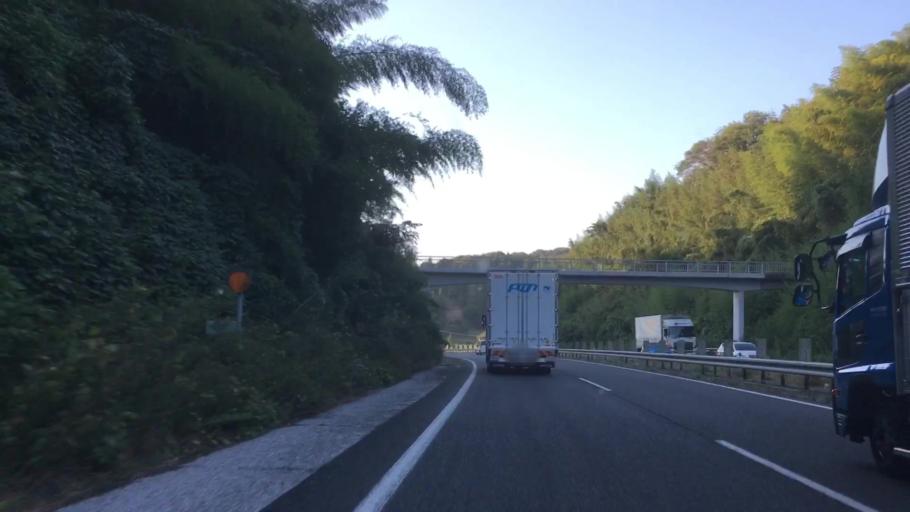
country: JP
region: Yamaguchi
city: Onoda
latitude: 34.1132
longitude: 131.1334
